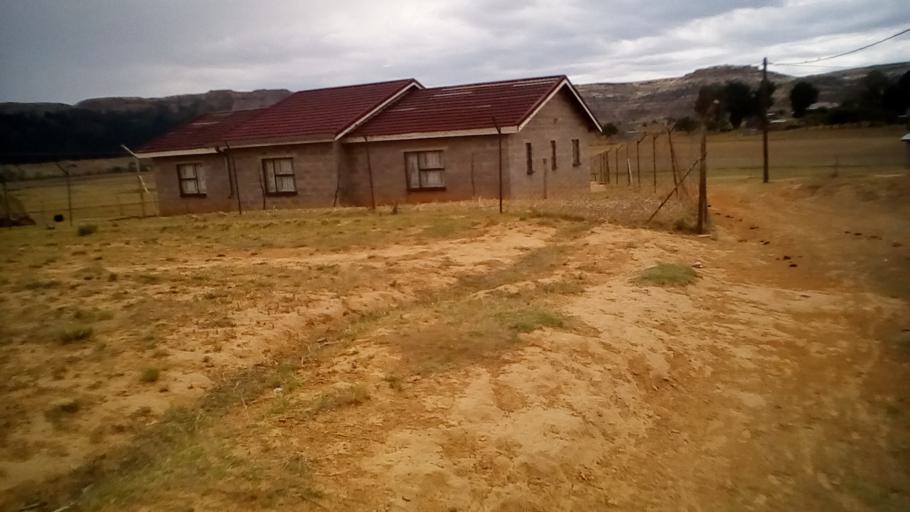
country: LS
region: Leribe
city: Leribe
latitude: -29.0269
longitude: 28.0207
